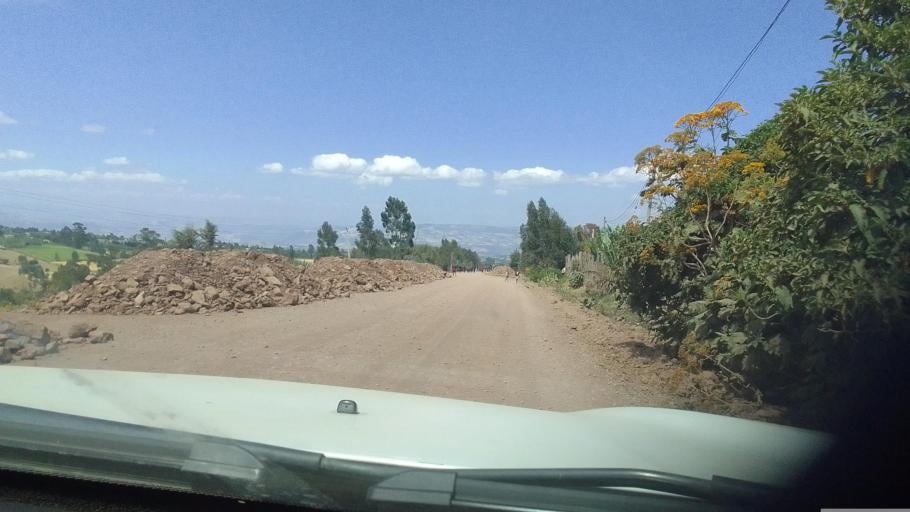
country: ET
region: Oromiya
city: Hagere Hiywet
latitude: 8.8577
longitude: 37.8918
